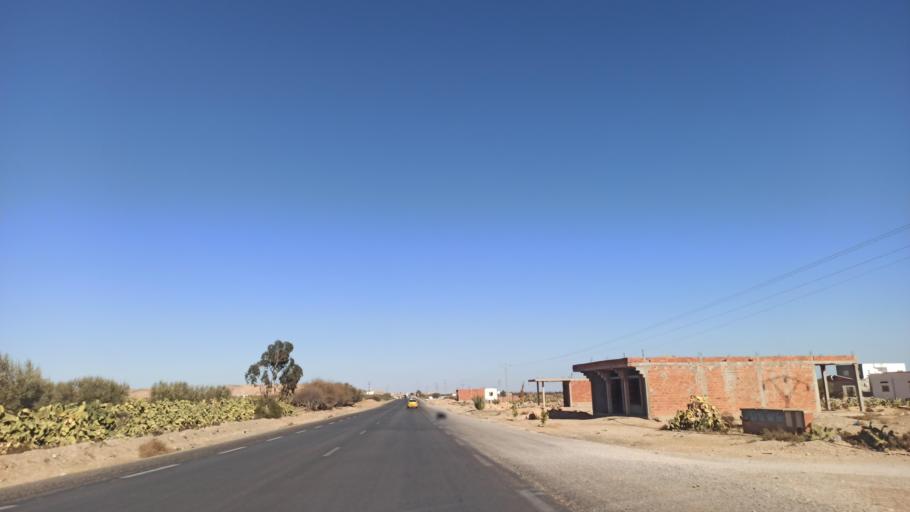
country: TN
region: Sidi Bu Zayd
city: Bi'r al Hufayy
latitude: 34.8998
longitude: 9.1745
